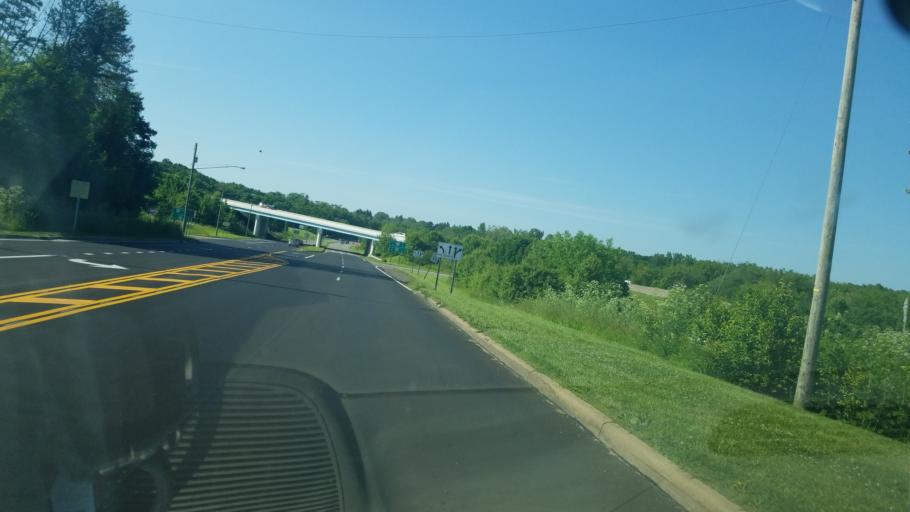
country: US
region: Ohio
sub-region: Wayne County
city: Wooster
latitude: 40.8363
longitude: -81.9293
